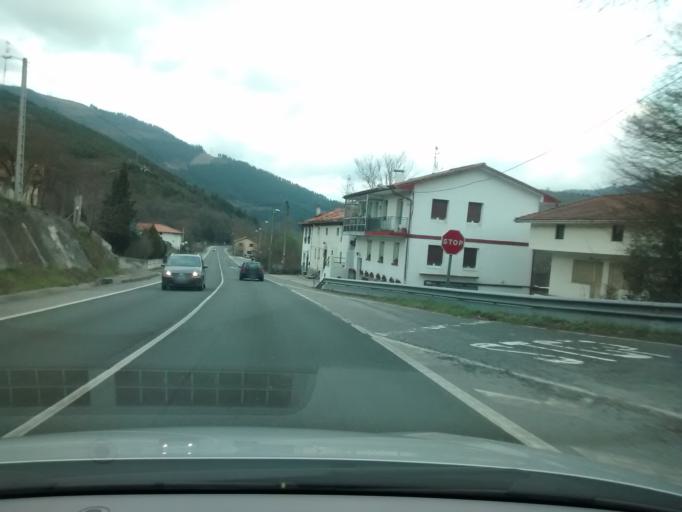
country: ES
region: Basque Country
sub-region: Bizkaia
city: Balmaseda
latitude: 43.1652
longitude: -3.2308
